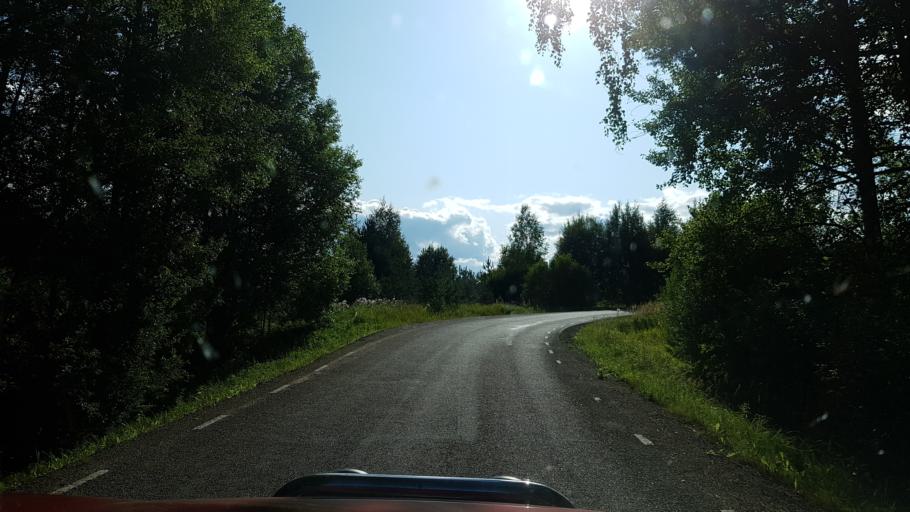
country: EE
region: Vorumaa
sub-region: Voru linn
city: Voru
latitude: 57.9232
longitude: 27.0364
